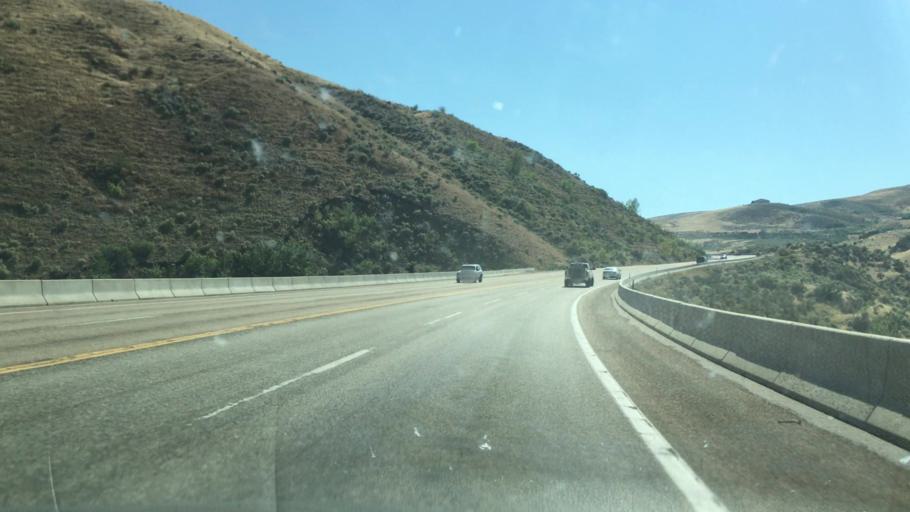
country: US
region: Idaho
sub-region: Ada County
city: Eagle
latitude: 43.8538
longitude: -116.2223
